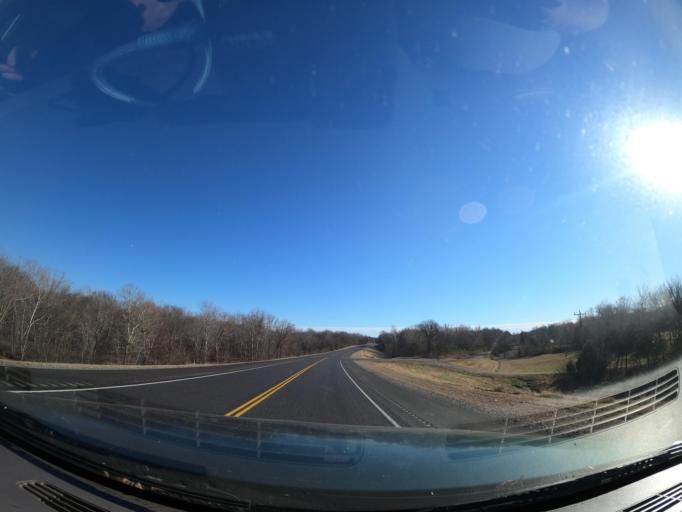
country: US
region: Oklahoma
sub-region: McIntosh County
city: Eufaula
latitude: 35.2666
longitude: -95.5824
